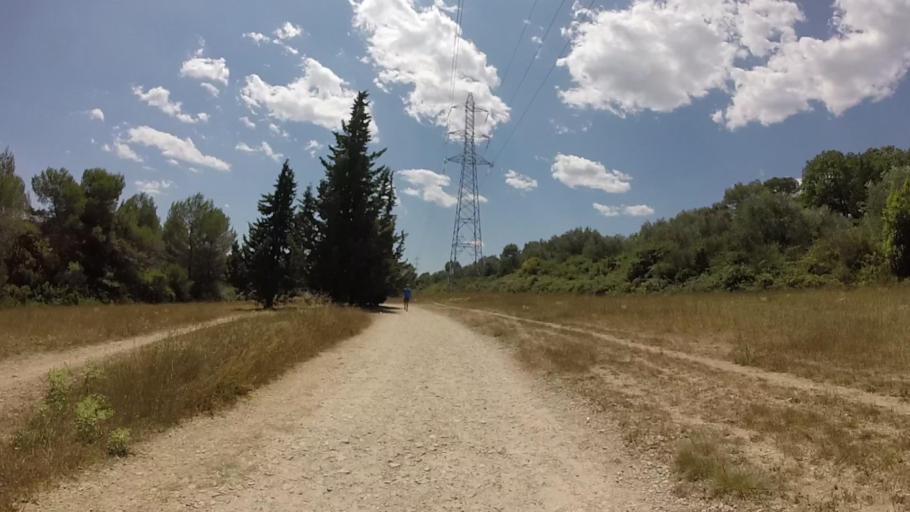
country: FR
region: Provence-Alpes-Cote d'Azur
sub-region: Departement des Alpes-Maritimes
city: Mougins
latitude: 43.5972
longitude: 7.0086
